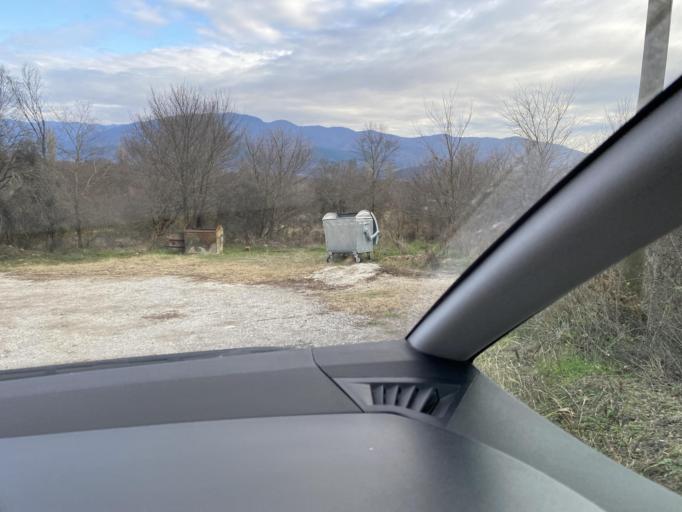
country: MK
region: Opstina Rankovce
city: Rankovce
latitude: 42.1833
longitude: 22.1107
